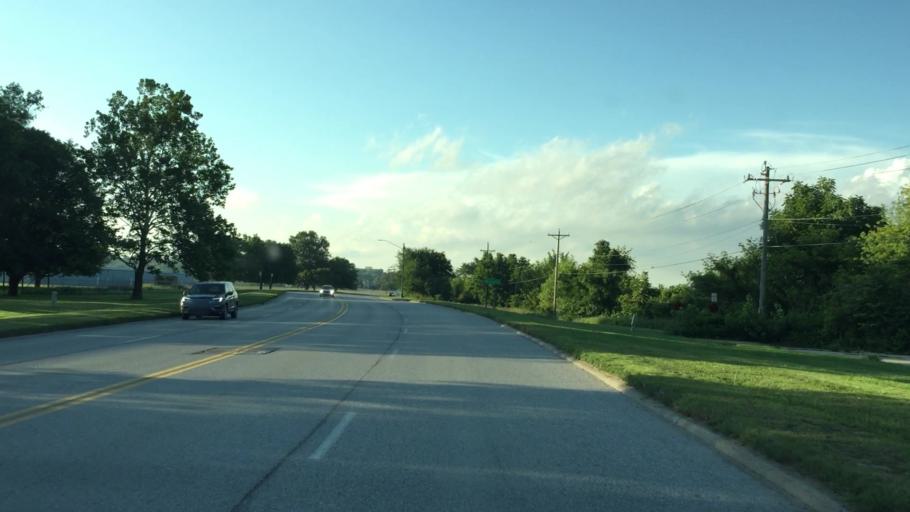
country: US
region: Iowa
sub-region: Johnson County
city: Iowa City
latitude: 41.6386
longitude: -91.5386
